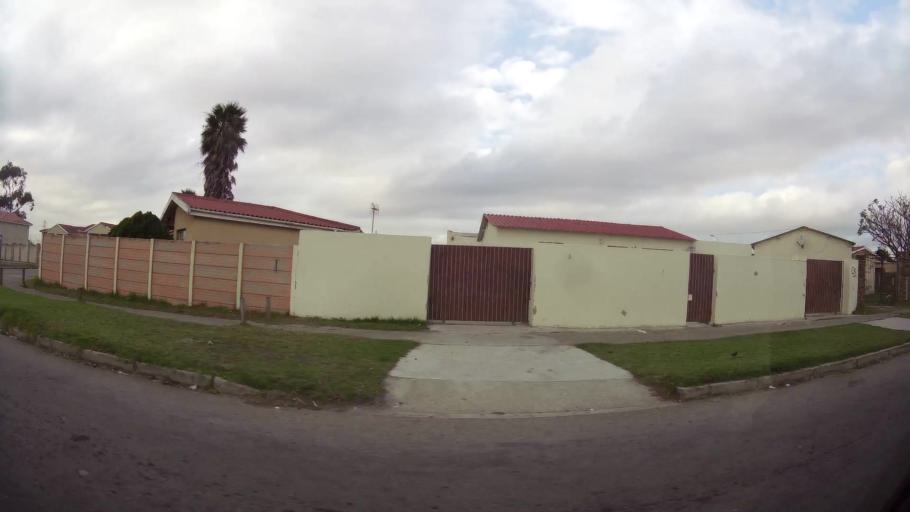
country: ZA
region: Eastern Cape
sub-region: Nelson Mandela Bay Metropolitan Municipality
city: Port Elizabeth
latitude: -33.9168
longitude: 25.5558
